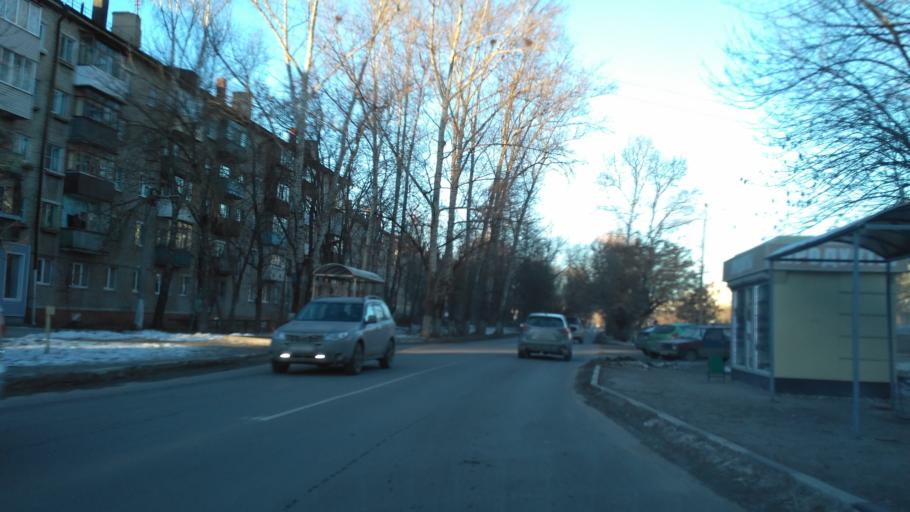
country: RU
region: Tula
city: Tula
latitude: 54.2097
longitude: 37.5956
